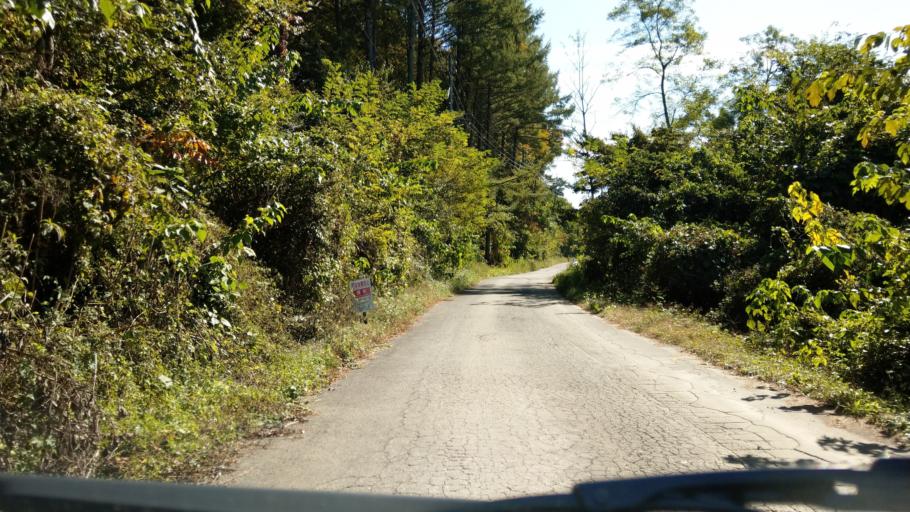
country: JP
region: Nagano
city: Komoro
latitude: 36.3549
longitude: 138.4037
